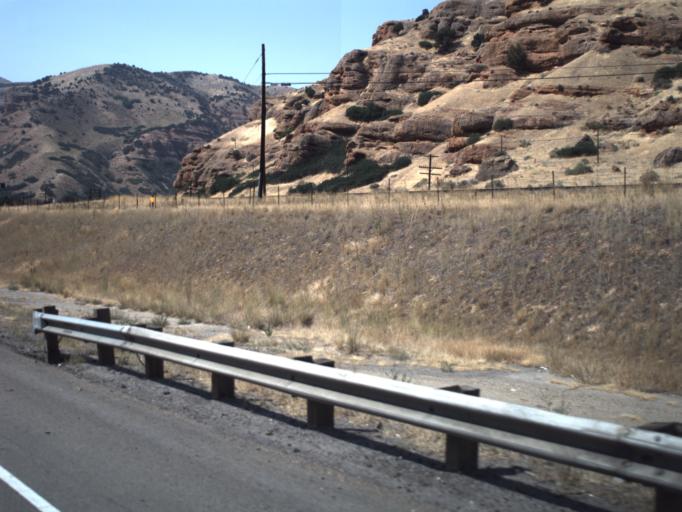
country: US
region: Utah
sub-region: Summit County
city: Coalville
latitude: 40.9734
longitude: -111.4348
